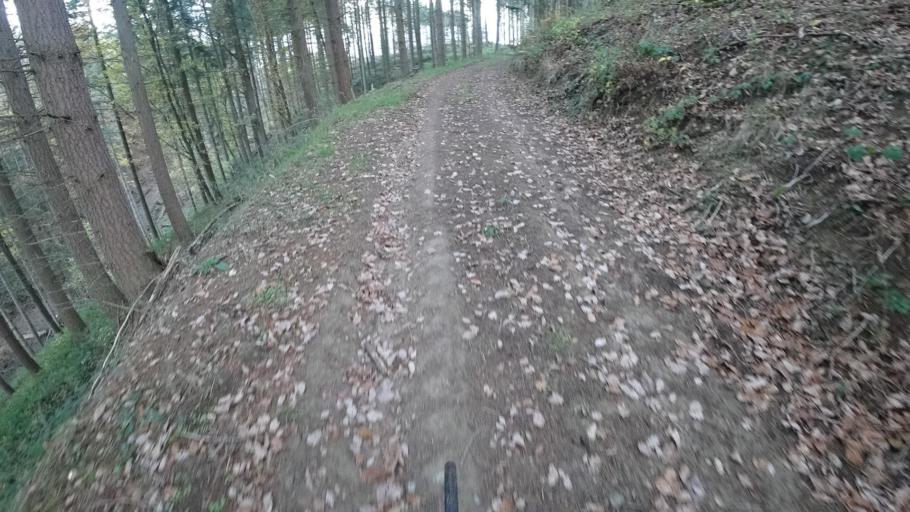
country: DE
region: Rheinland-Pfalz
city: Harscheid
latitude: 50.4664
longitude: 6.8920
